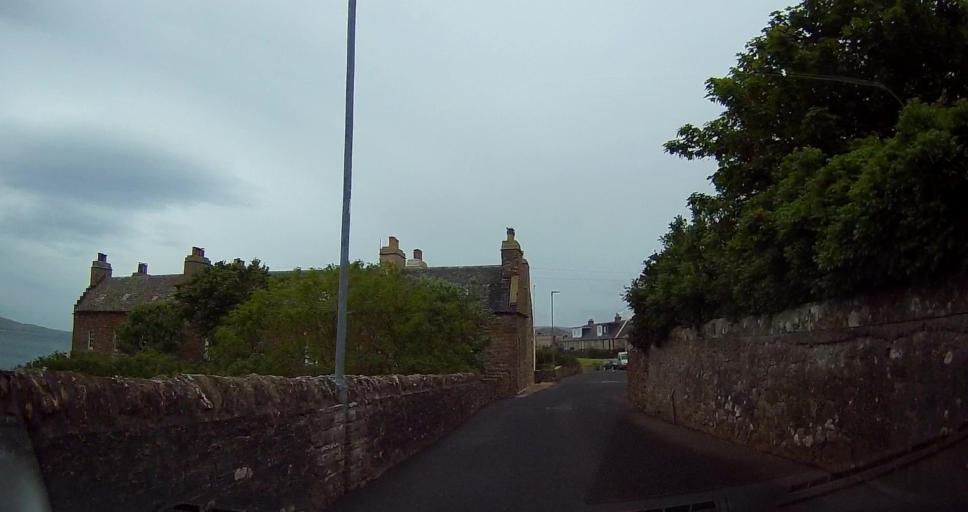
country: GB
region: Scotland
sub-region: Orkney Islands
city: Stromness
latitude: 58.9554
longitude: -3.3005
